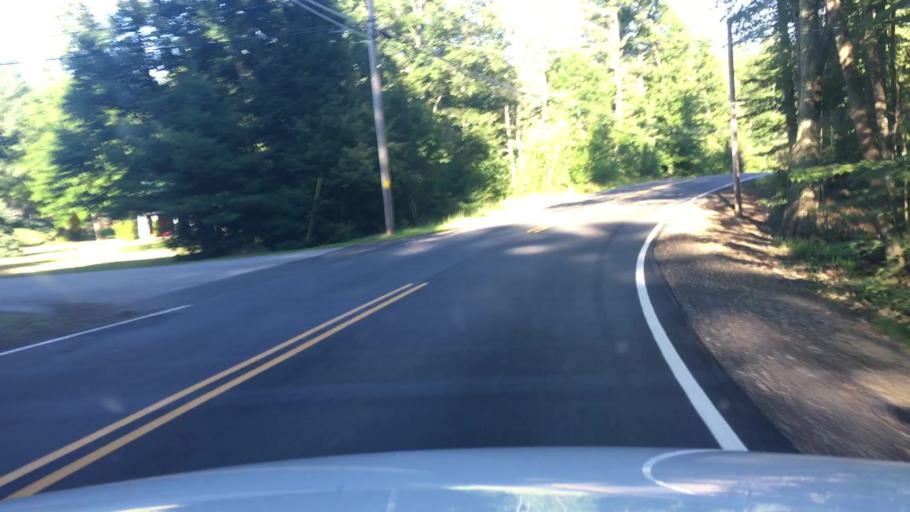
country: US
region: New Hampshire
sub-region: Rockingham County
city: Sandown
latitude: 42.9131
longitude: -71.1806
